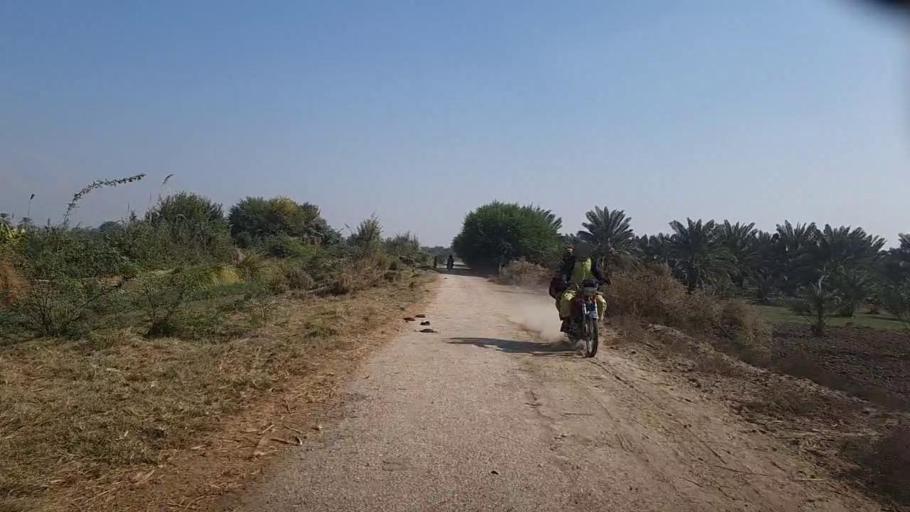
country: PK
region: Sindh
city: Bozdar
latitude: 27.1916
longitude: 68.6242
